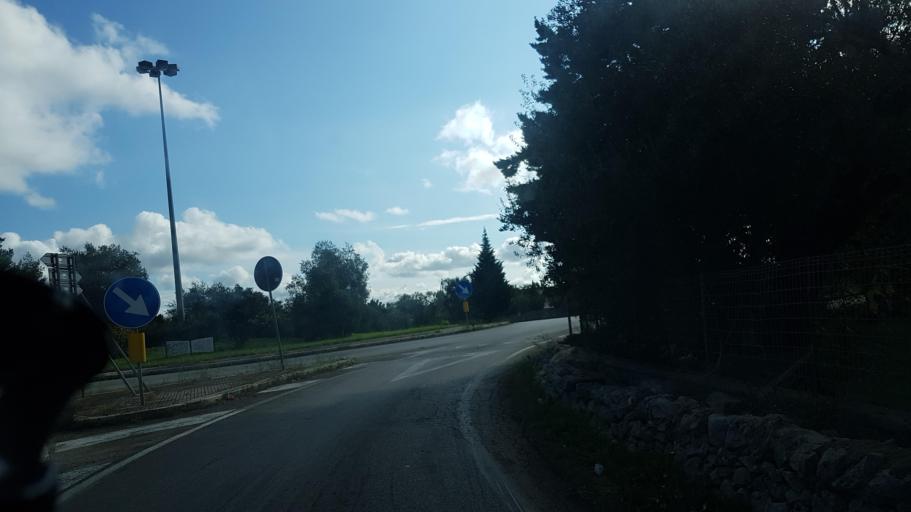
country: IT
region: Apulia
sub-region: Provincia di Brindisi
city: San Michele Salentino
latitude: 40.6468
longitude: 17.6074
